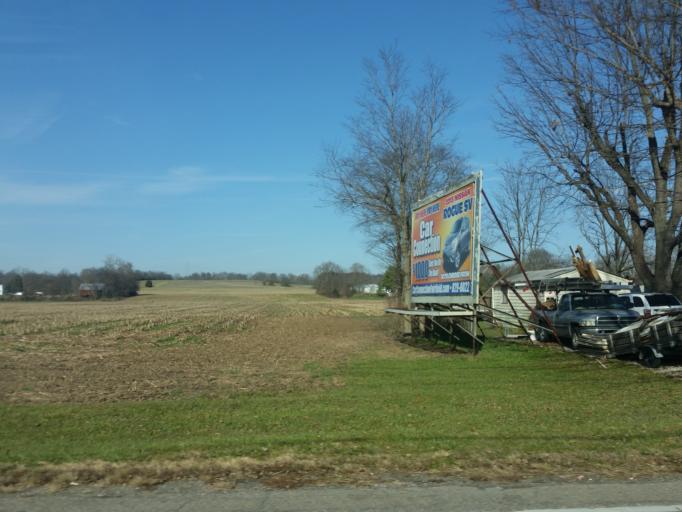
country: US
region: Ohio
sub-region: Butler County
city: Ross
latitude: 39.3913
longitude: -84.6569
